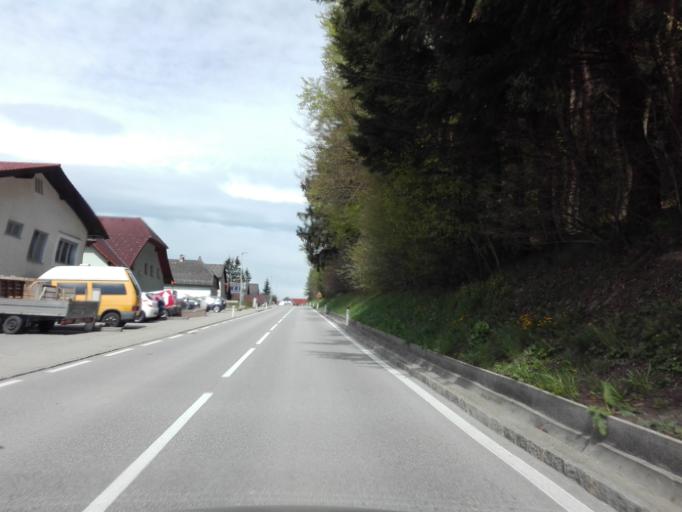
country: AT
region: Upper Austria
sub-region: Politischer Bezirk Urfahr-Umgebung
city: Eidenberg
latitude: 48.3481
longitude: 14.2419
